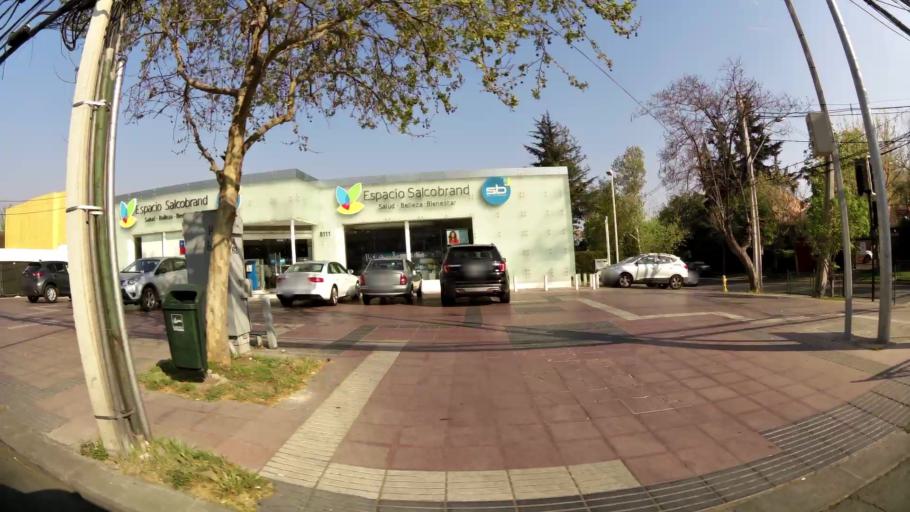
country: CL
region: Santiago Metropolitan
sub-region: Provincia de Santiago
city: Villa Presidente Frei, Nunoa, Santiago, Chile
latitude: -33.3856
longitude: -70.5560
